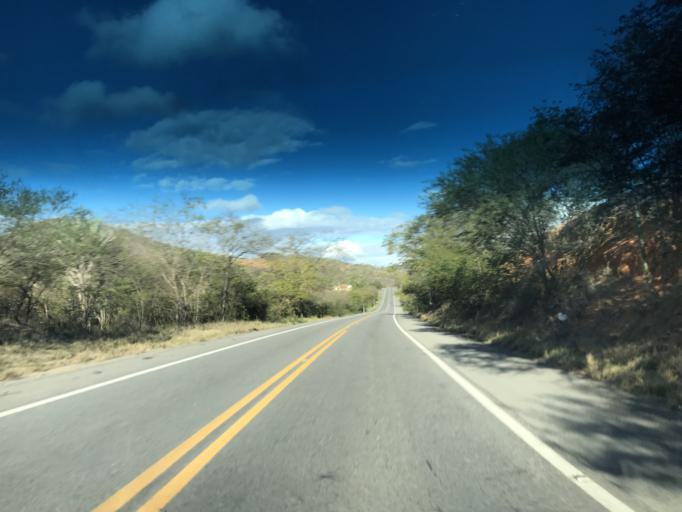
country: BR
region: Bahia
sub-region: Itaberaba
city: Itaberaba
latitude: -12.5091
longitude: -40.4694
